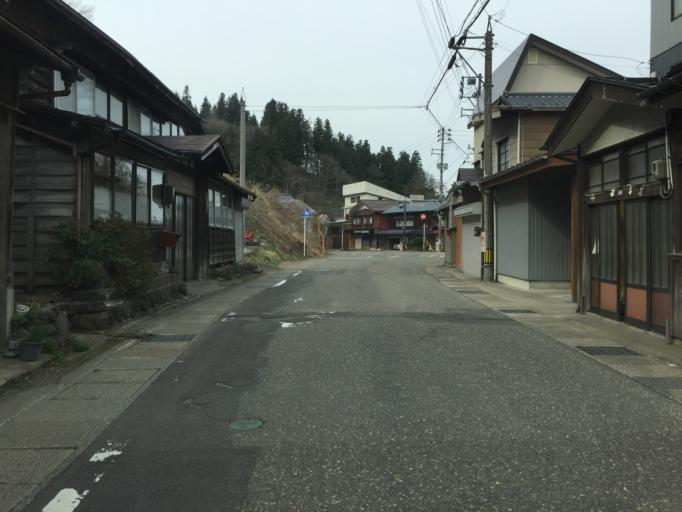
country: JP
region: Niigata
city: Tochio-honcho
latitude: 37.4714
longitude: 138.9922
